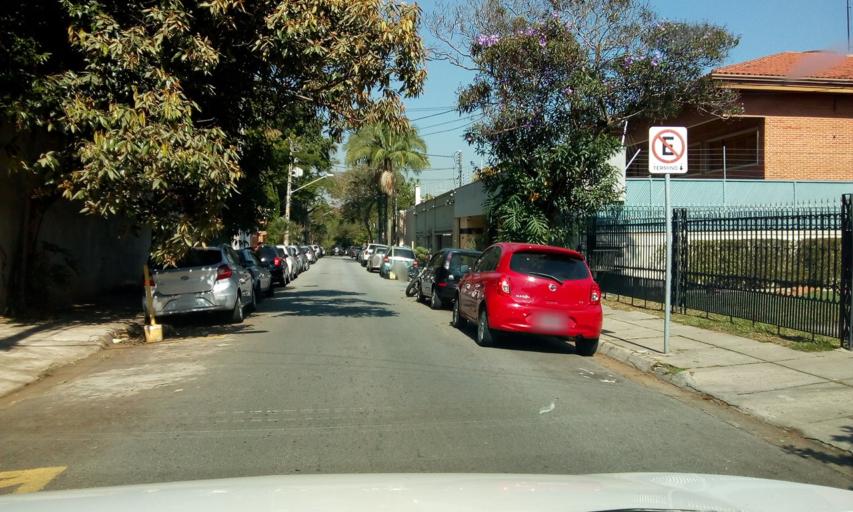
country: BR
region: Sao Paulo
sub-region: Taboao Da Serra
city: Taboao da Serra
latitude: -23.5961
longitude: -46.7095
